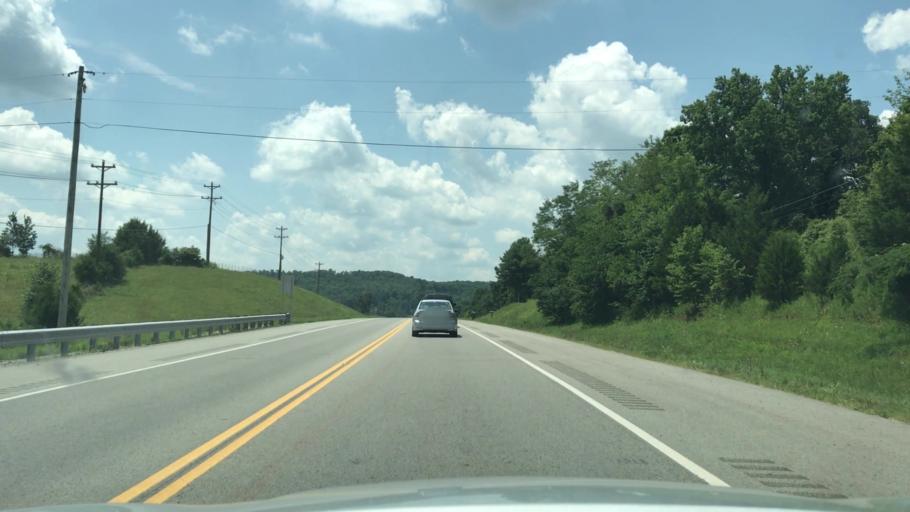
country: US
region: Tennessee
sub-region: Overton County
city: Livingston
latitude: 36.4140
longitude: -85.2872
